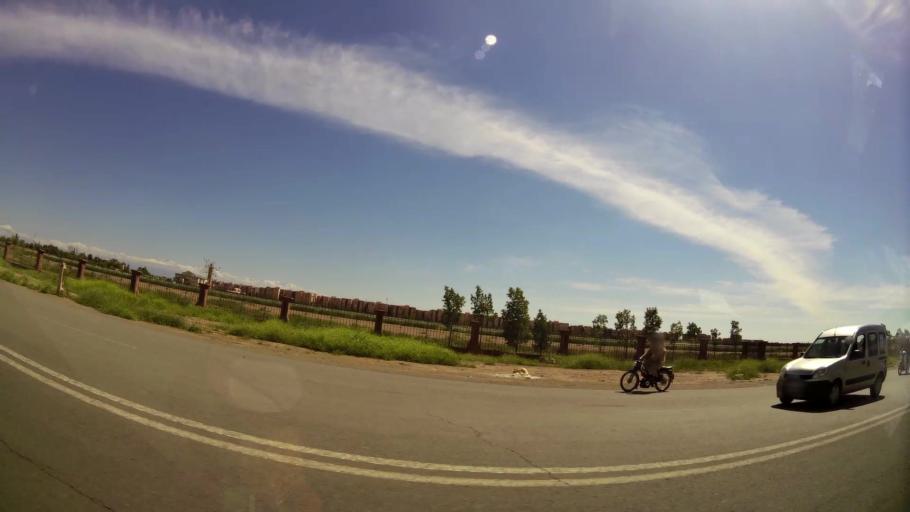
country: MA
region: Marrakech-Tensift-Al Haouz
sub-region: Marrakech
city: Marrakesh
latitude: 31.6402
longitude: -8.0965
